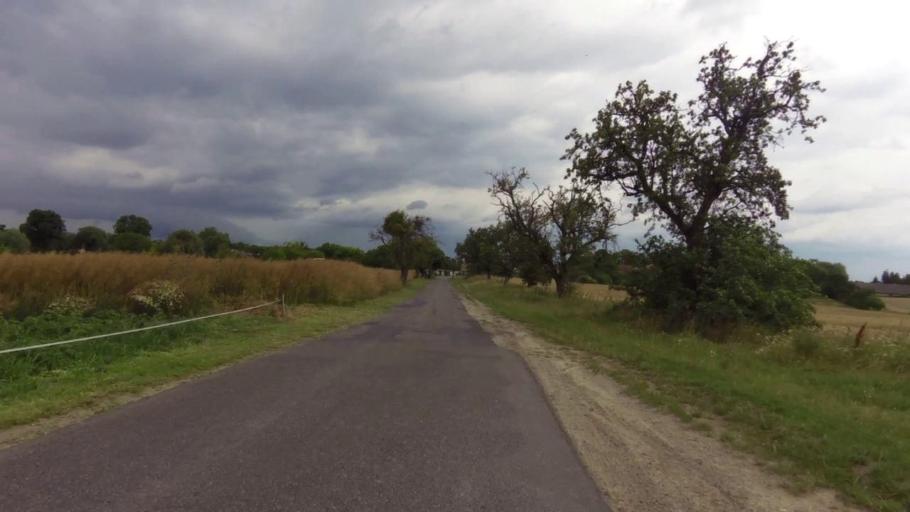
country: PL
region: West Pomeranian Voivodeship
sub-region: Powiat gryfinski
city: Chojna
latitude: 52.9064
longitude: 14.4289
